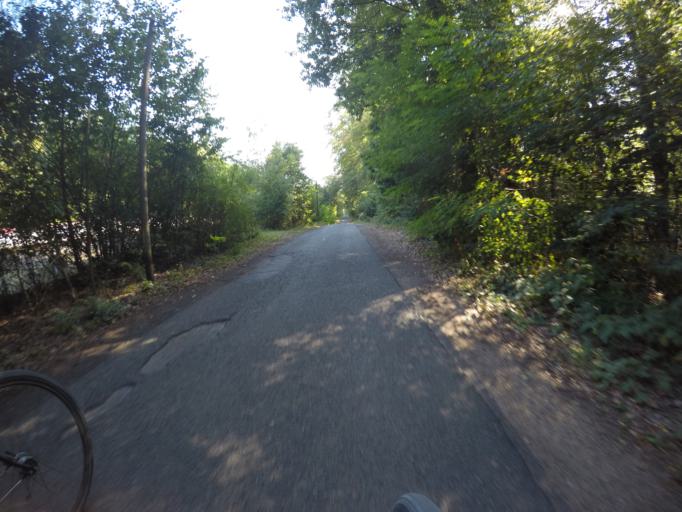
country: DE
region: Hesse
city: Dreieich
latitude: 50.0309
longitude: 8.6620
